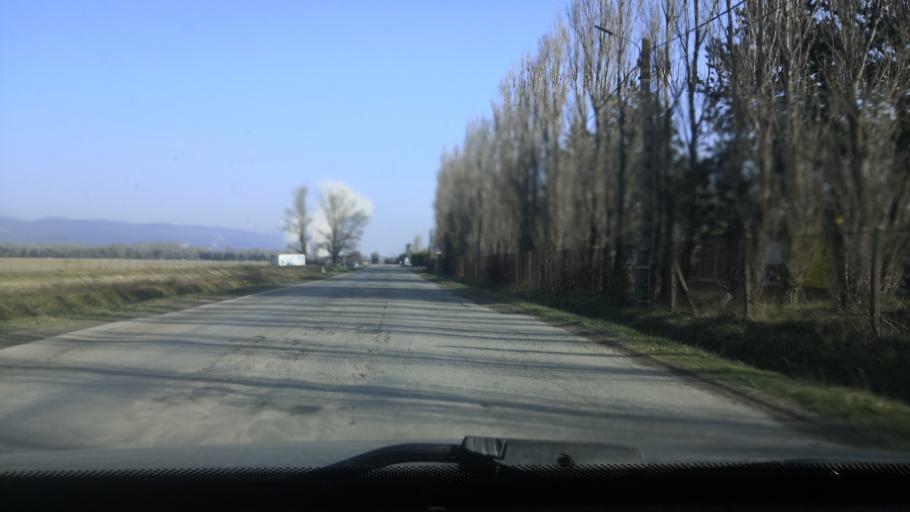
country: FR
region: Rhone-Alpes
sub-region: Departement de la Drome
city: Ancone
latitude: 44.5770
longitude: 4.7402
